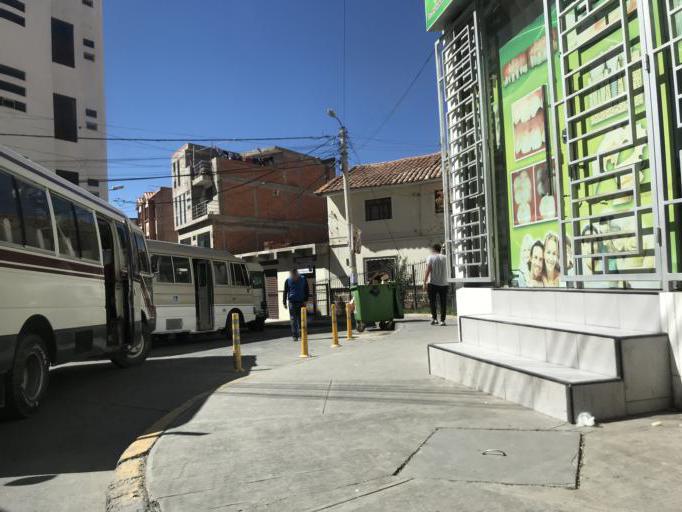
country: BO
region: Chuquisaca
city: Sucre
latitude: -19.0348
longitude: -65.2566
